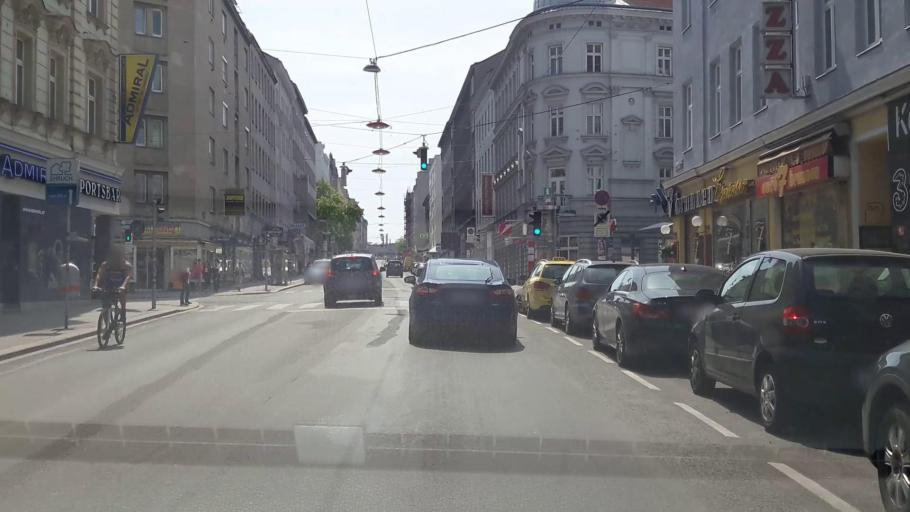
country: AT
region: Vienna
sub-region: Wien Stadt
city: Vienna
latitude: 48.1860
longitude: 16.3538
